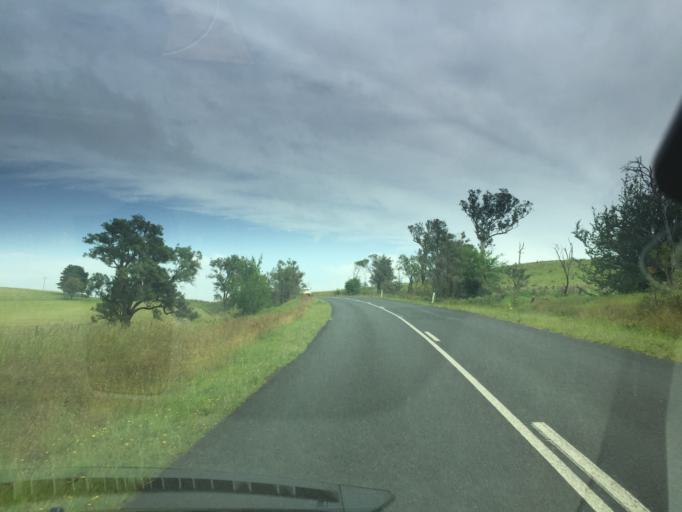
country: AU
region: New South Wales
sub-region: Bega Valley
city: Bega
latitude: -36.7320
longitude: 149.6375
